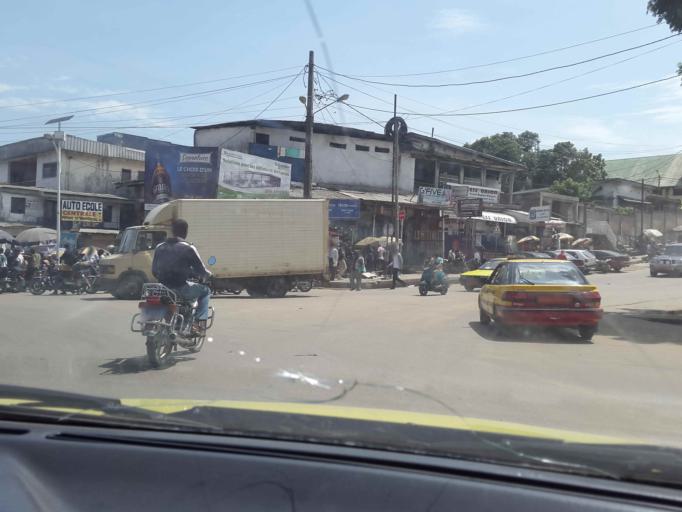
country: CM
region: Littoral
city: Douala
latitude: 4.0642
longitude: 9.7071
